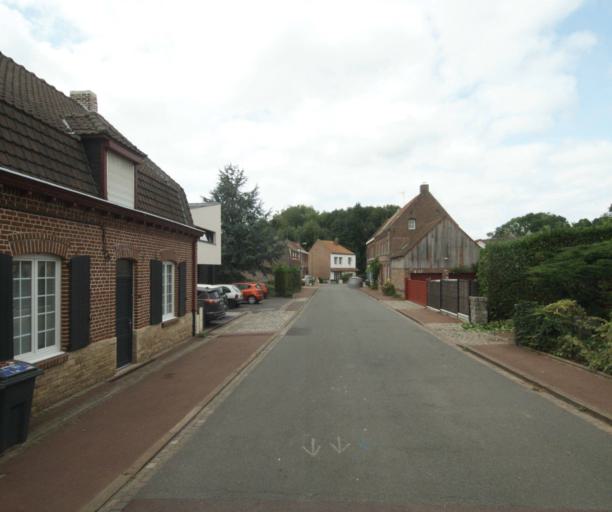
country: FR
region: Nord-Pas-de-Calais
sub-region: Departement du Nord
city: Gruson
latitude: 50.5930
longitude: 3.2070
